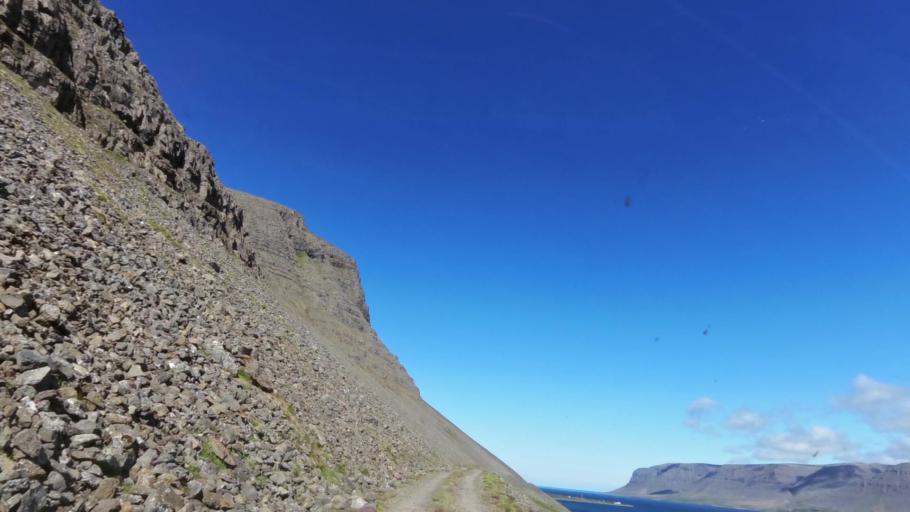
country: IS
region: West
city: Olafsvik
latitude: 65.6280
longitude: -23.9043
